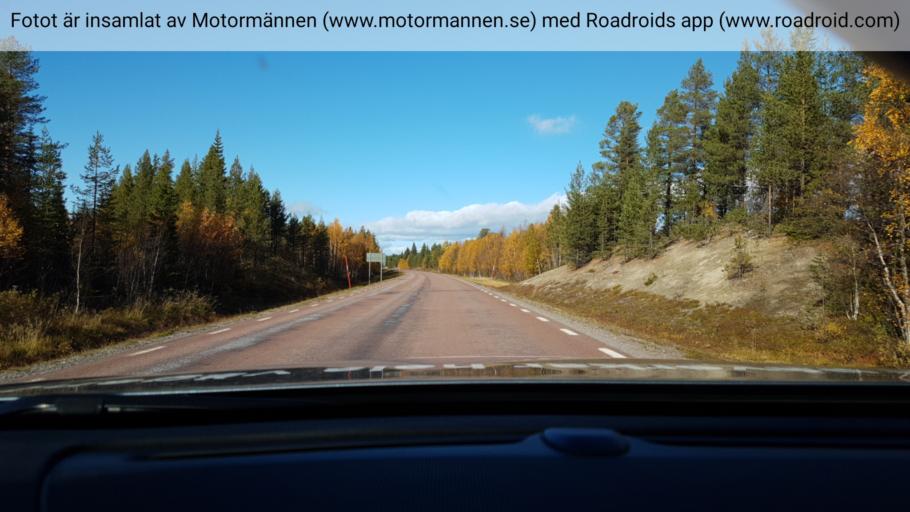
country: SE
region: Norrbotten
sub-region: Arjeplogs Kommun
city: Arjeplog
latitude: 65.9904
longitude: 18.1825
